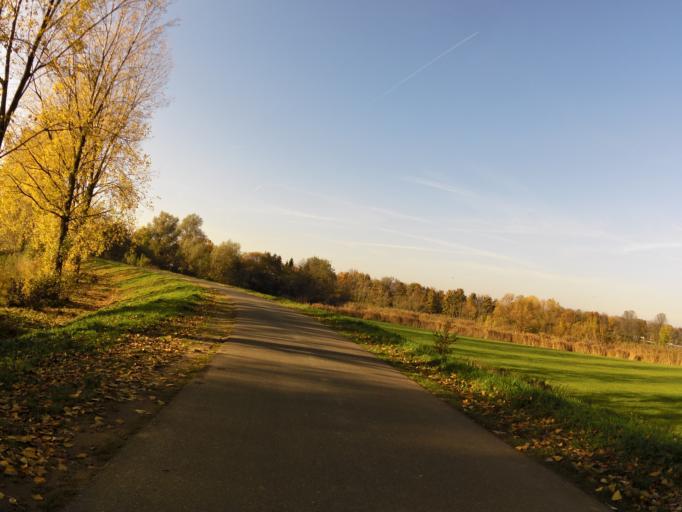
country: NL
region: North Brabant
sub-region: Gemeente 's-Hertogenbosch
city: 's-Hertogenbosch
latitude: 51.7140
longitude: 5.2838
